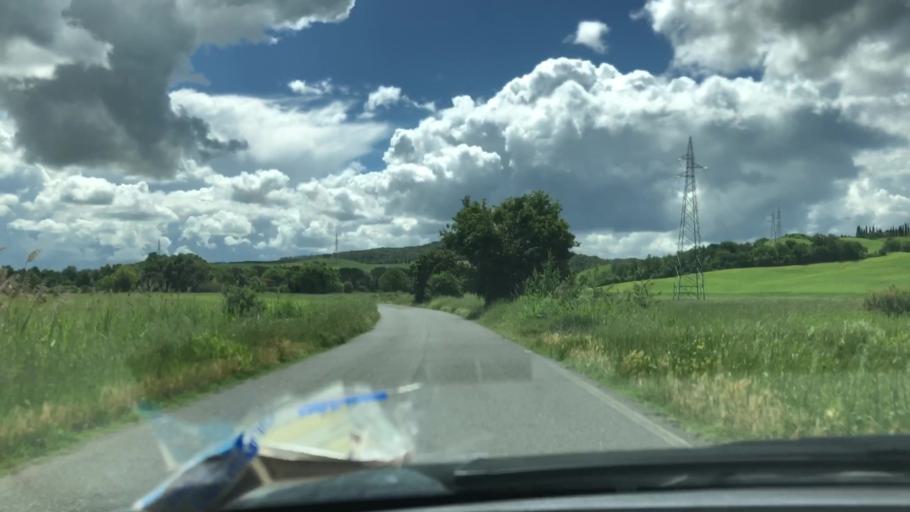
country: IT
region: Tuscany
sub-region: Province of Pisa
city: Saline
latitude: 43.3519
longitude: 10.7881
